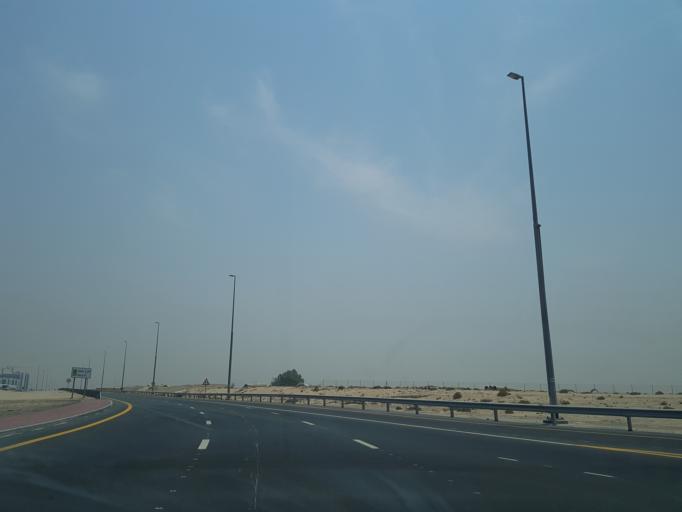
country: AE
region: Dubai
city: Dubai
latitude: 25.0233
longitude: 55.2399
